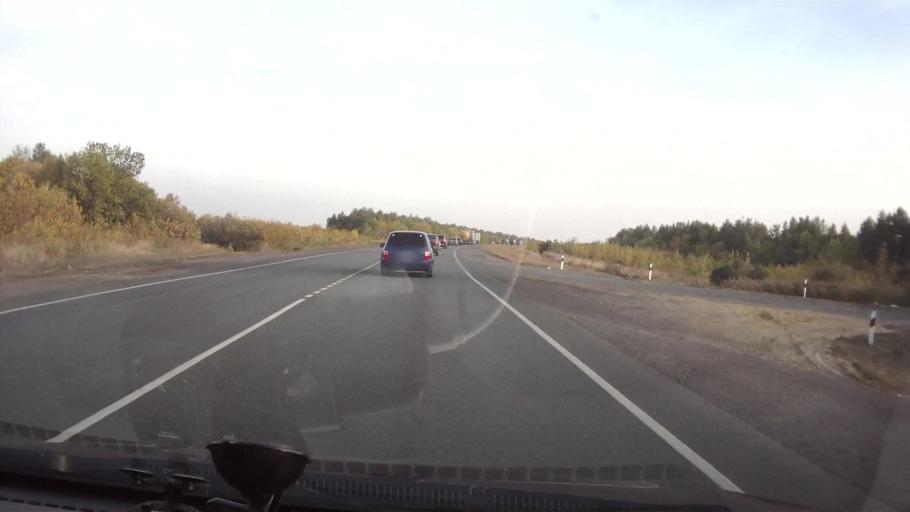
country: RU
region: Saratov
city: Sokolovyy
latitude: 51.5328
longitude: 45.8021
